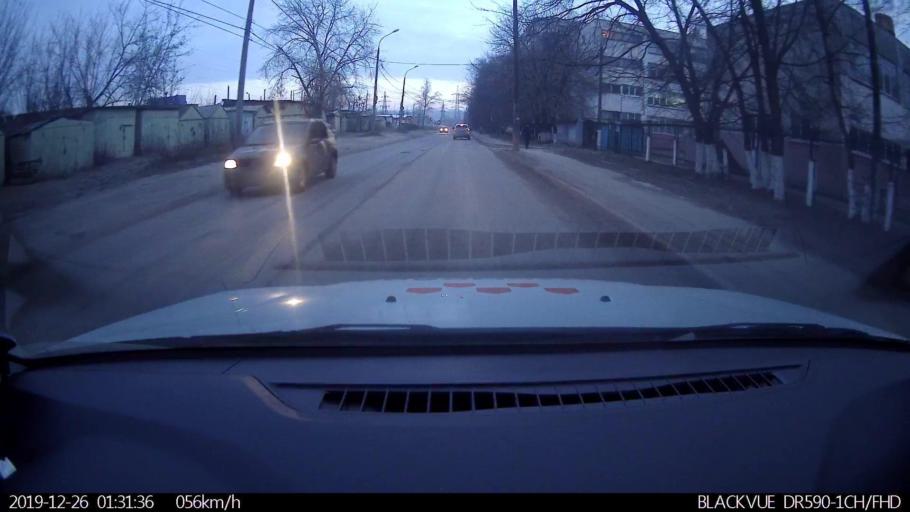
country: RU
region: Nizjnij Novgorod
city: Nizhniy Novgorod
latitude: 56.2665
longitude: 43.9003
